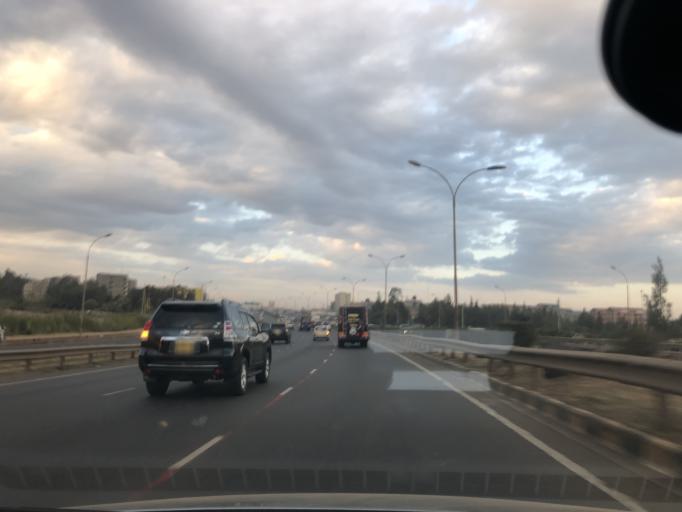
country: KE
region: Kiambu
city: Kiambu
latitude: -1.2096
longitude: 36.9111
